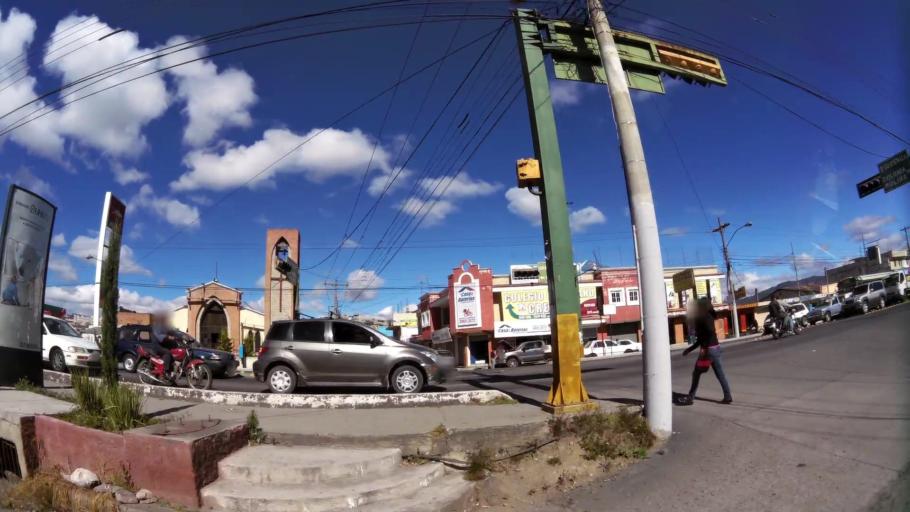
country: GT
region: Quetzaltenango
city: Quetzaltenango
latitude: 14.8362
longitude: -91.5101
